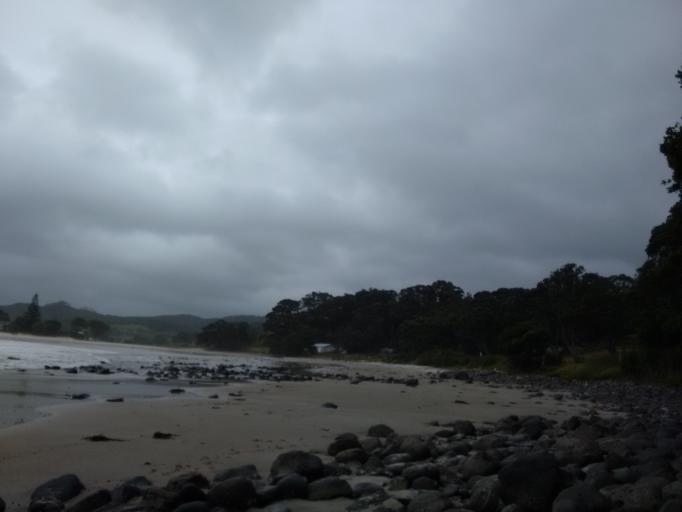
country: NZ
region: Waikato
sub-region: Thames-Coromandel District
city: Coromandel
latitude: -36.7045
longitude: 175.6097
